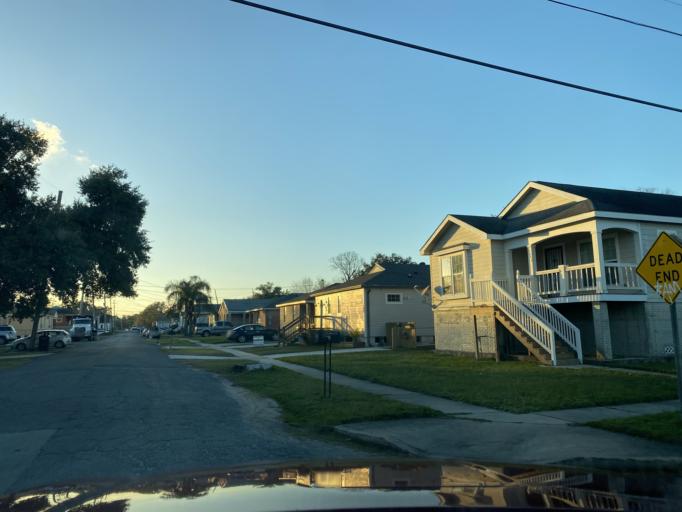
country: US
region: Louisiana
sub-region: Orleans Parish
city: New Orleans
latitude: 30.0259
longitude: -90.0499
